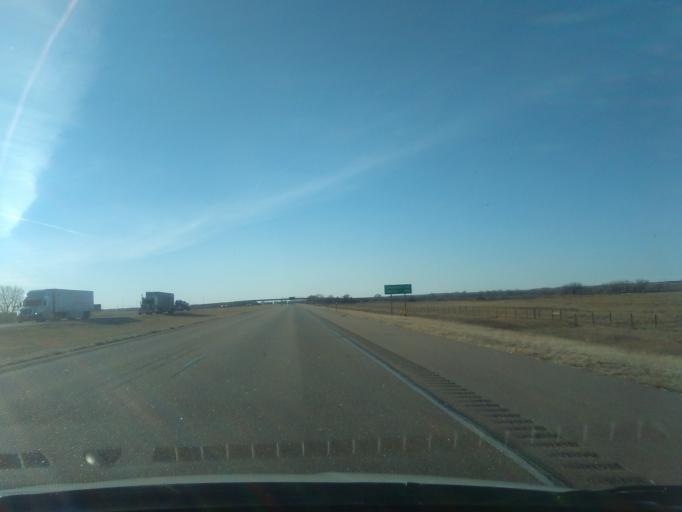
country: US
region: Colorado
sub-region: Sedgwick County
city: Julesburg
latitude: 41.0390
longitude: -102.1181
